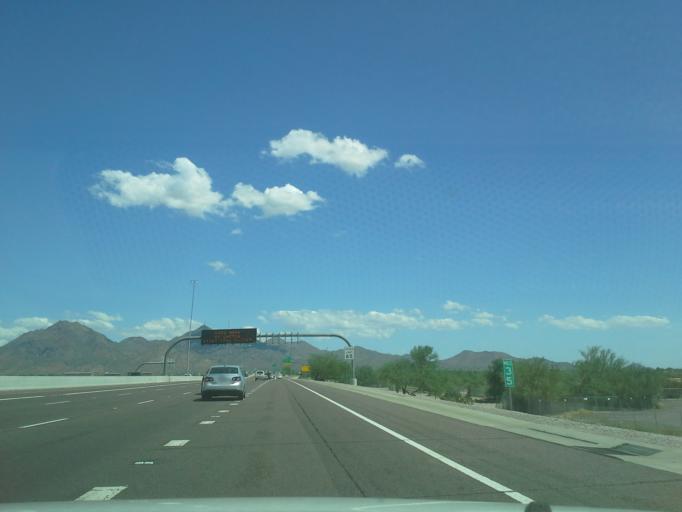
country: US
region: Arizona
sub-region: Maricopa County
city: Paradise Valley
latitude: 33.6564
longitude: -111.9175
